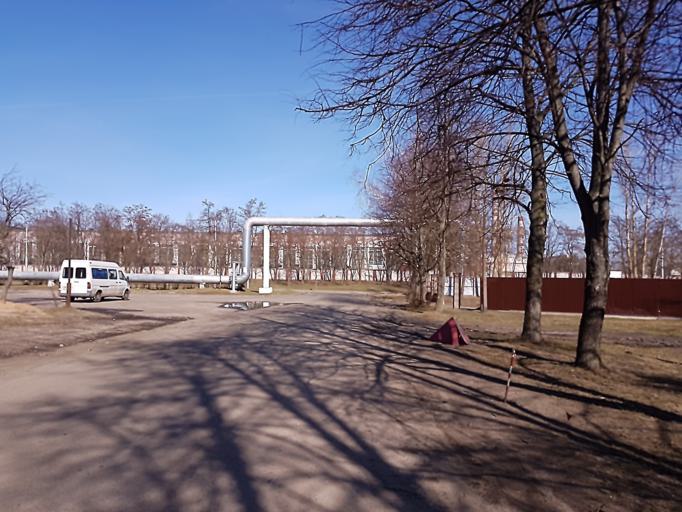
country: BY
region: Mogilev
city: Babruysk
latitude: 53.1804
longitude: 29.2076
